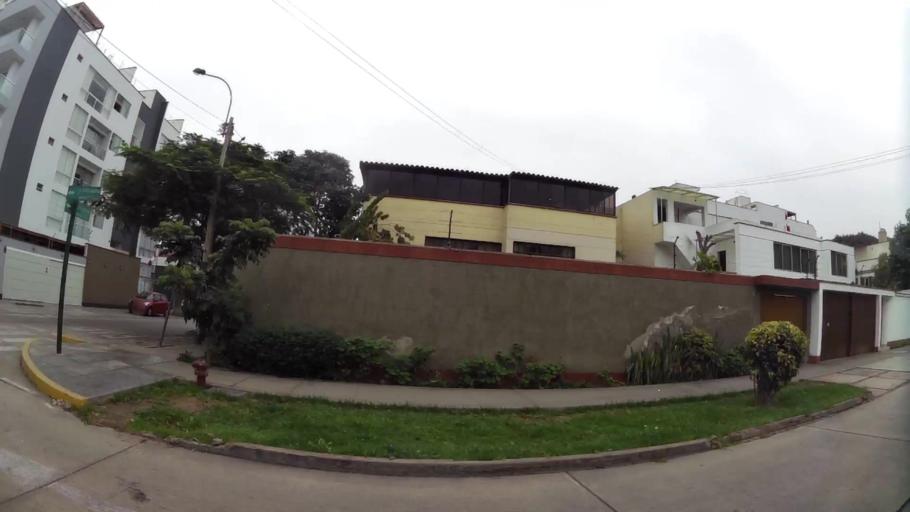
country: PE
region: Lima
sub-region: Lima
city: Surco
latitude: -12.1391
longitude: -76.9972
